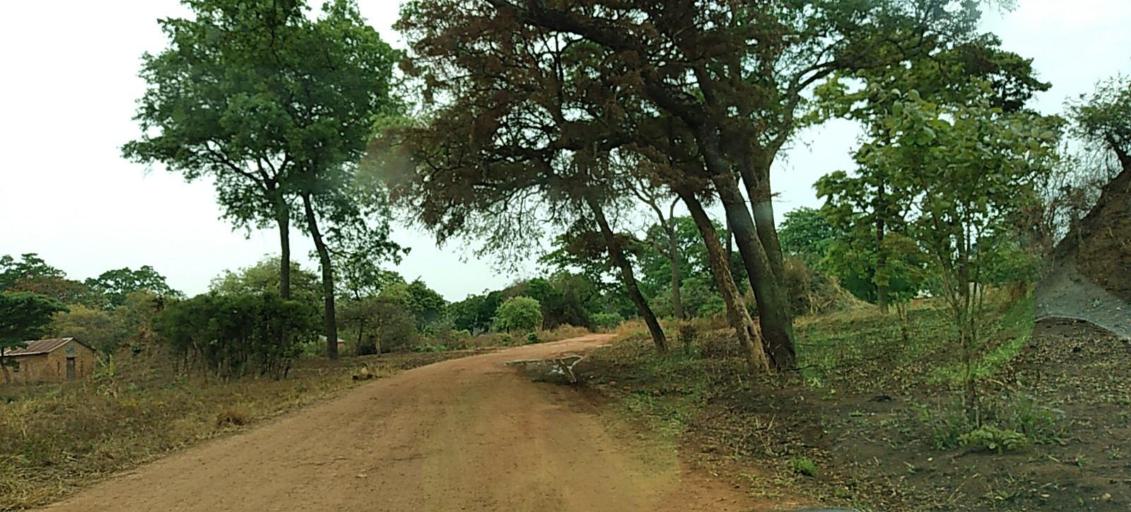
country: ZM
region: North-Western
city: Solwezi
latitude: -12.3444
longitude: 26.5287
